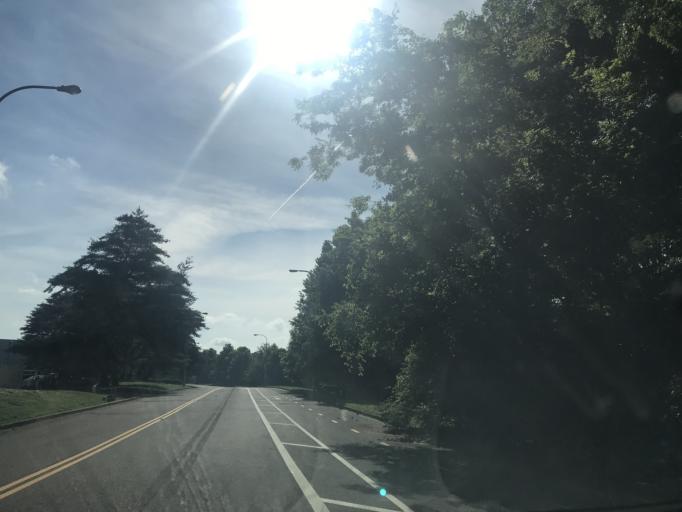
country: US
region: Tennessee
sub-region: Davidson County
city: Nashville
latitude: 36.1931
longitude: -86.8226
